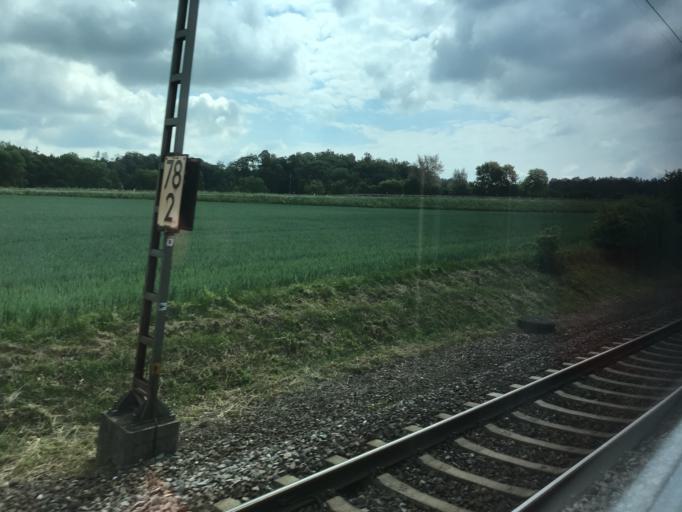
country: DE
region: Baden-Wuerttemberg
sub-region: Tuebingen Region
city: Westerstetten
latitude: 48.5062
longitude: 9.9501
